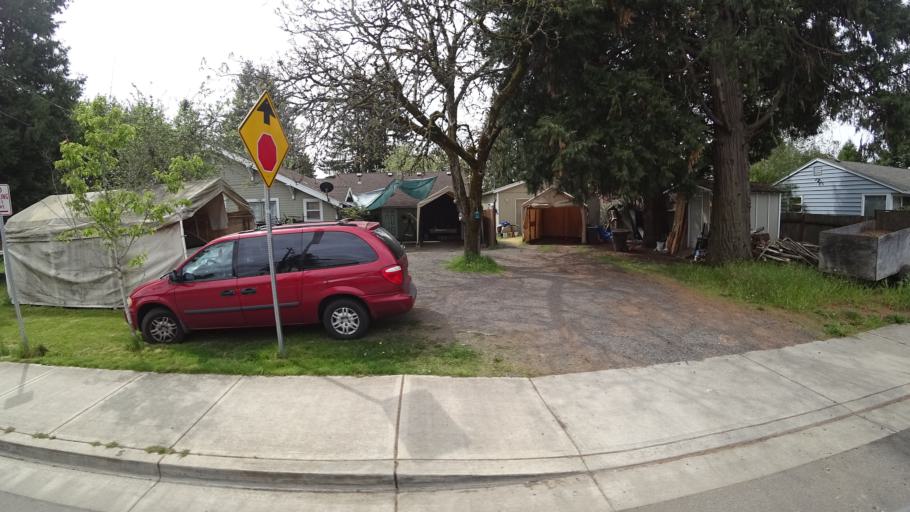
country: US
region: Oregon
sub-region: Washington County
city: Hillsboro
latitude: 45.5279
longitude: -122.9944
